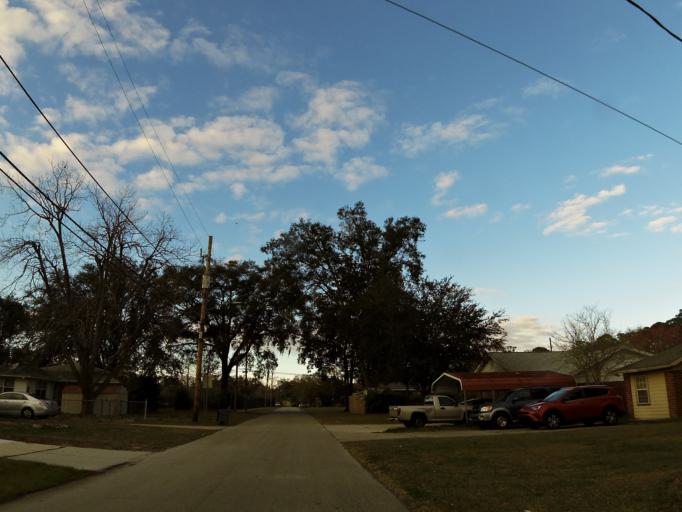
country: US
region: Florida
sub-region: Duval County
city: Jacksonville
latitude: 30.2969
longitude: -81.7284
